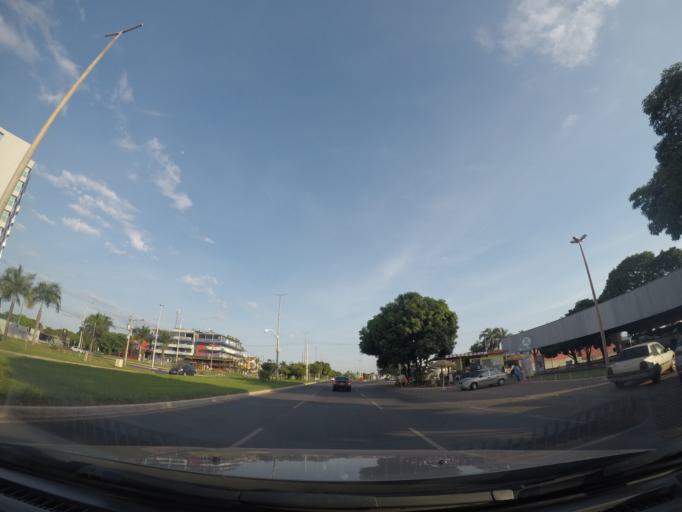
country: BR
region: Federal District
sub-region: Brasilia
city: Brasilia
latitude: -15.8406
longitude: -47.9662
